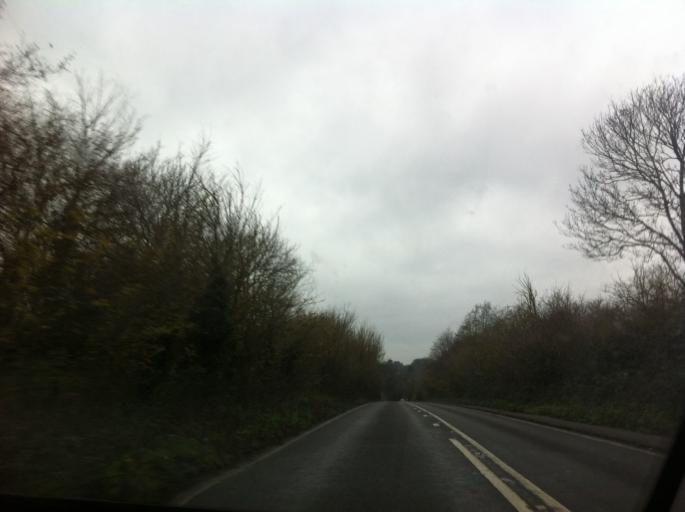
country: GB
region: England
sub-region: Northamptonshire
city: Earls Barton
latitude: 52.2661
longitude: -0.7182
